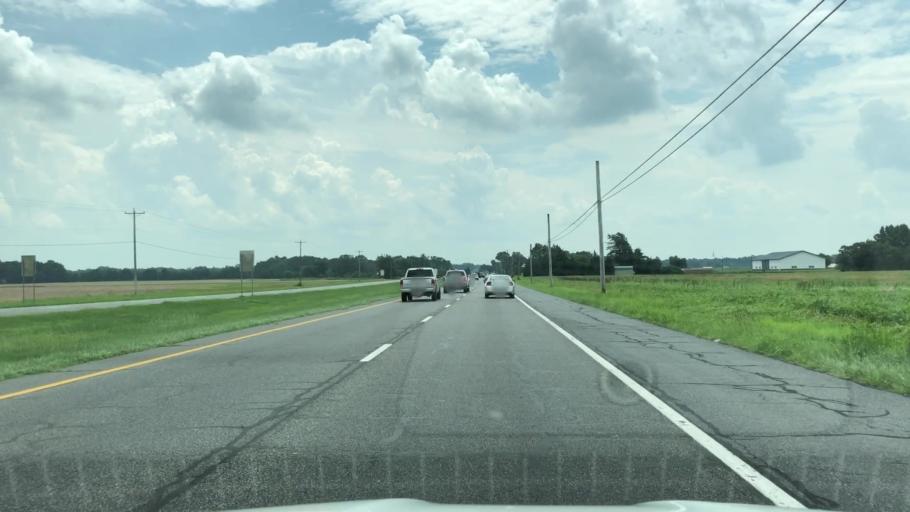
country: US
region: Delaware
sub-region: Kent County
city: Felton
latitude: 38.9996
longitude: -75.5693
